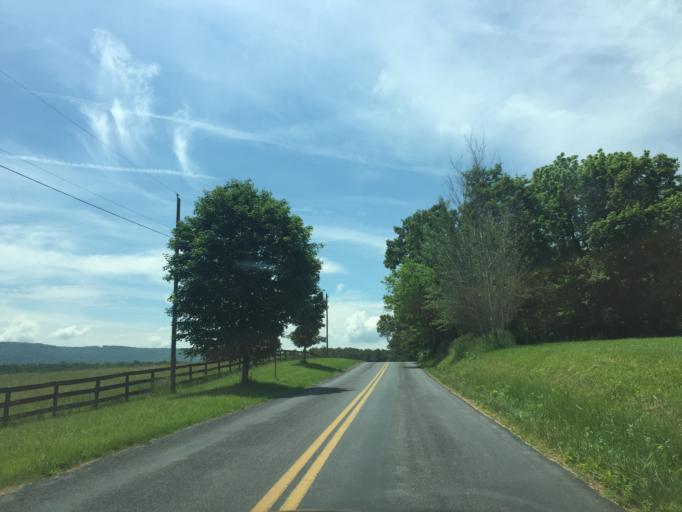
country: US
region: Virginia
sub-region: Warren County
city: Shenandoah Farms
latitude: 38.9748
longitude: -78.1247
